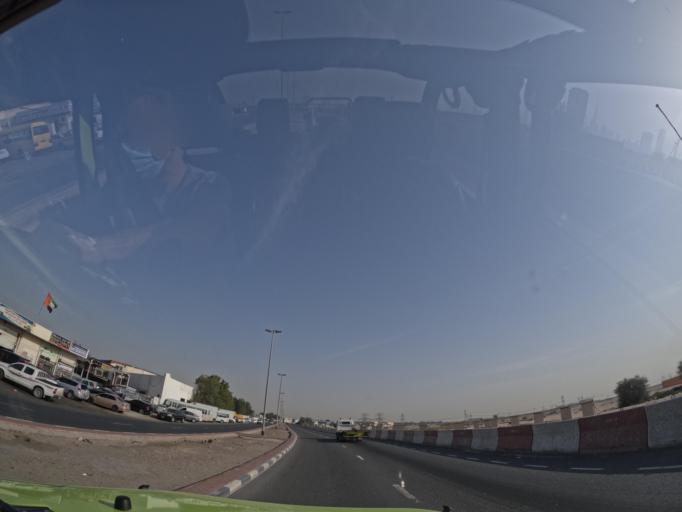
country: AE
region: Ash Shariqah
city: Sharjah
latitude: 25.1796
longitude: 55.3297
